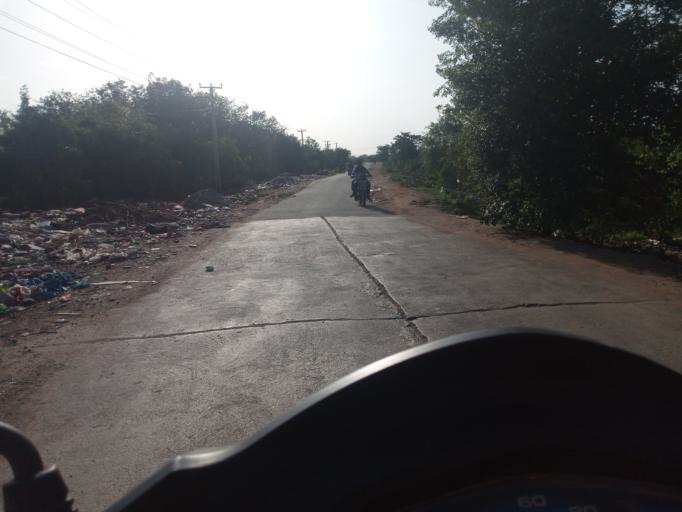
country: IN
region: Telangana
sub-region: Rangareddi
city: Quthbullapur
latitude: 17.5510
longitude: 78.4218
